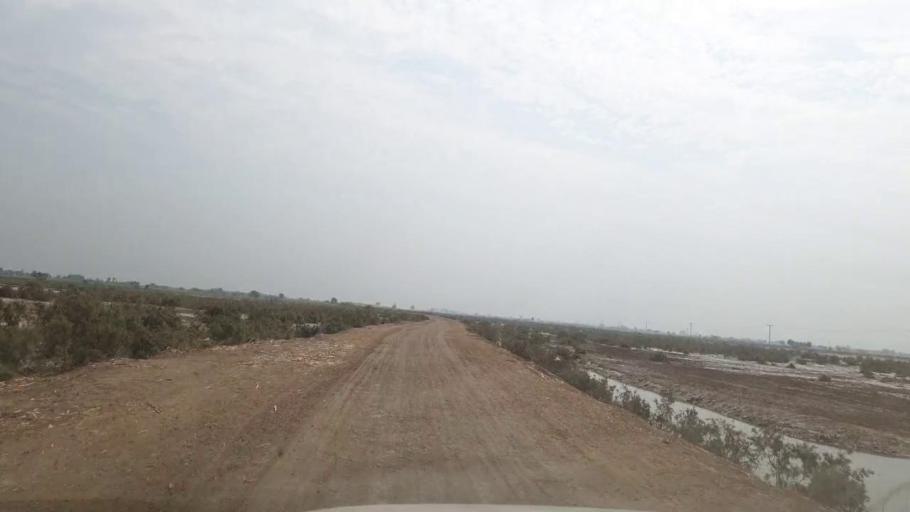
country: PK
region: Sindh
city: Mirpur Khas
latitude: 25.5479
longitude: 69.1250
